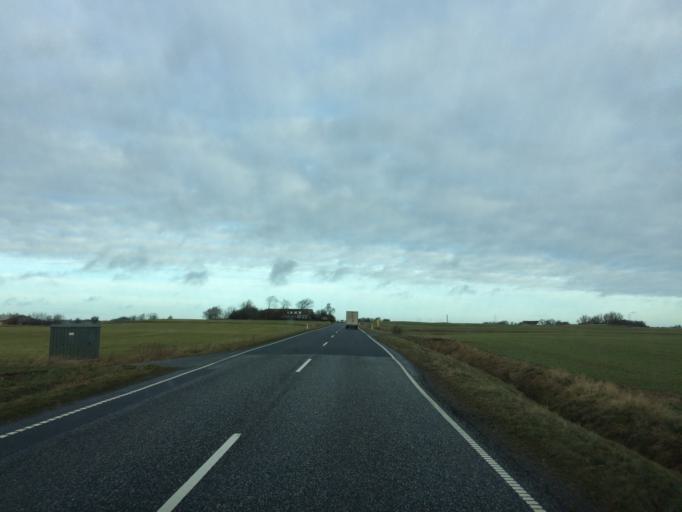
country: DK
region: Central Jutland
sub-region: Struer Kommune
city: Struer
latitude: 56.4577
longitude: 8.5421
